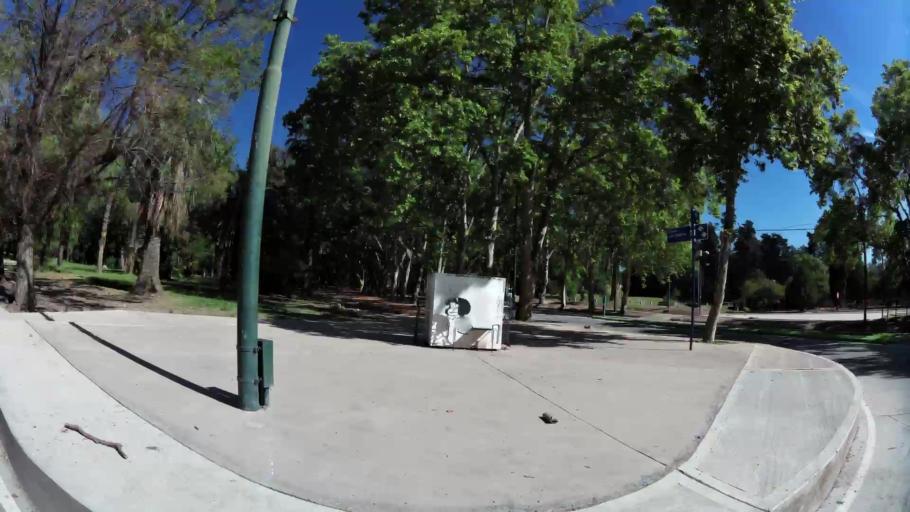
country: AR
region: Mendoza
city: Mendoza
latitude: -32.8885
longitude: -68.8710
